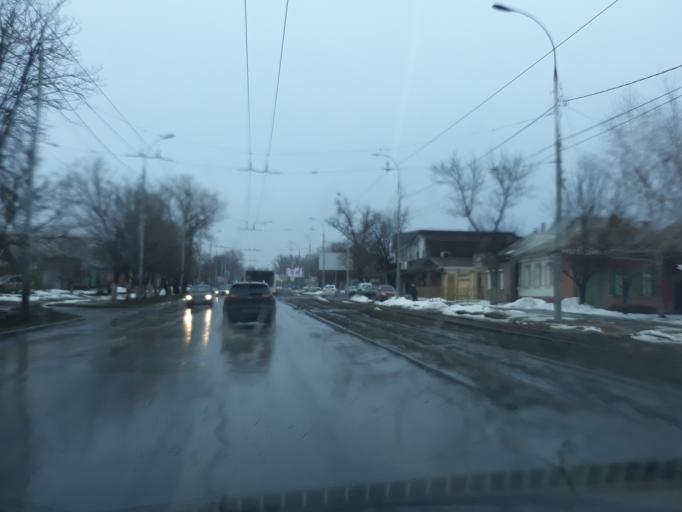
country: RU
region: Rostov
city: Taganrog
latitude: 47.2309
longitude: 38.9180
